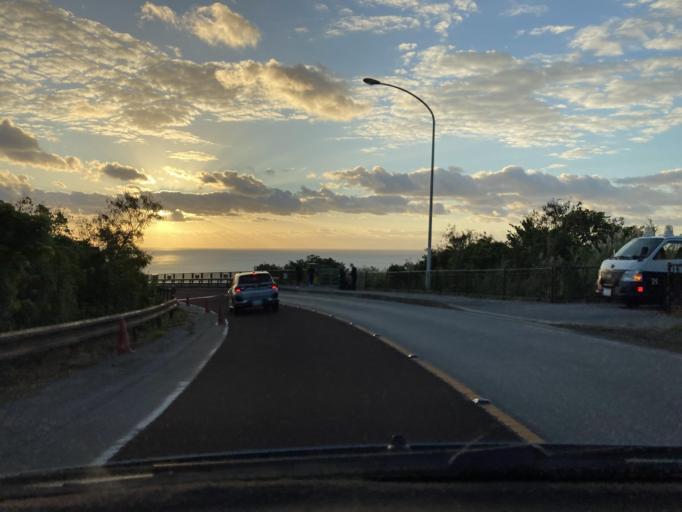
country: JP
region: Okinawa
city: Ginowan
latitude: 26.1648
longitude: 127.8163
